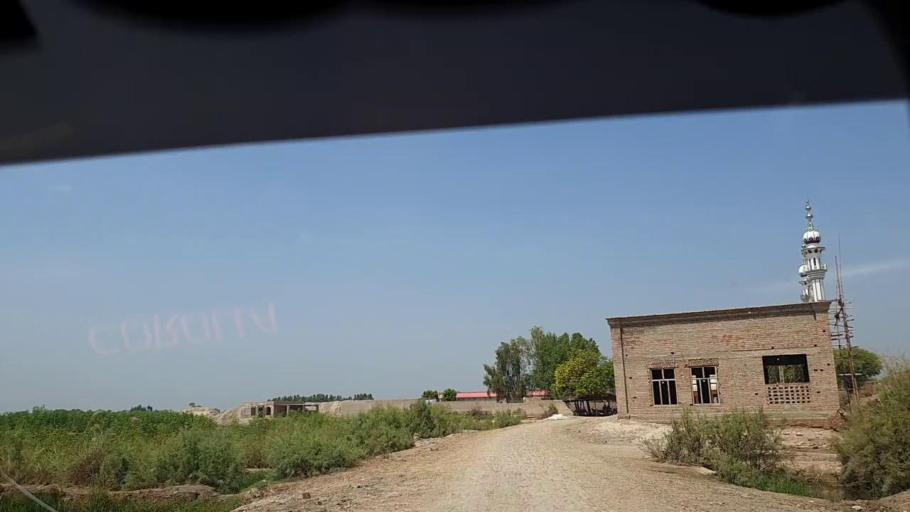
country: PK
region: Sindh
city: Ghauspur
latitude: 28.1754
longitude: 69.0673
